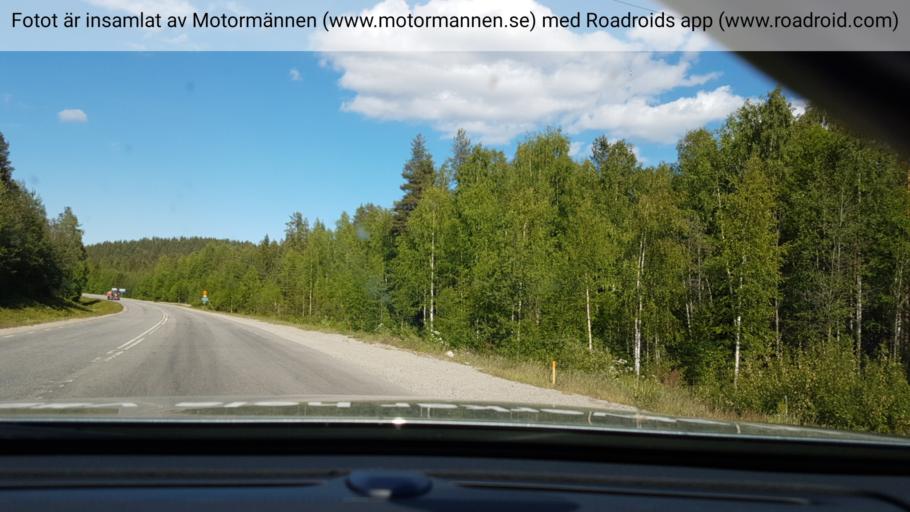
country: SE
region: Vaesterbotten
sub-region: Lycksele Kommun
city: Lycksele
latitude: 64.5759
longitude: 18.6524
